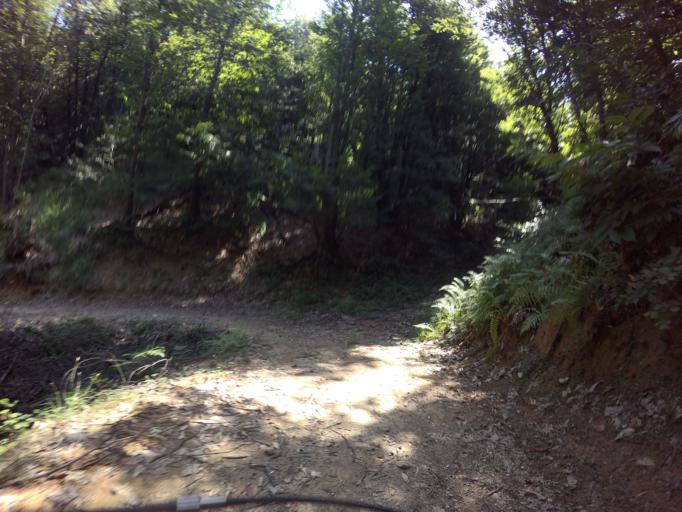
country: IT
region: Piedmont
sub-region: Provincia di Cuneo
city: Roccaforte Mondovi
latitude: 44.3261
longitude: 7.7135
